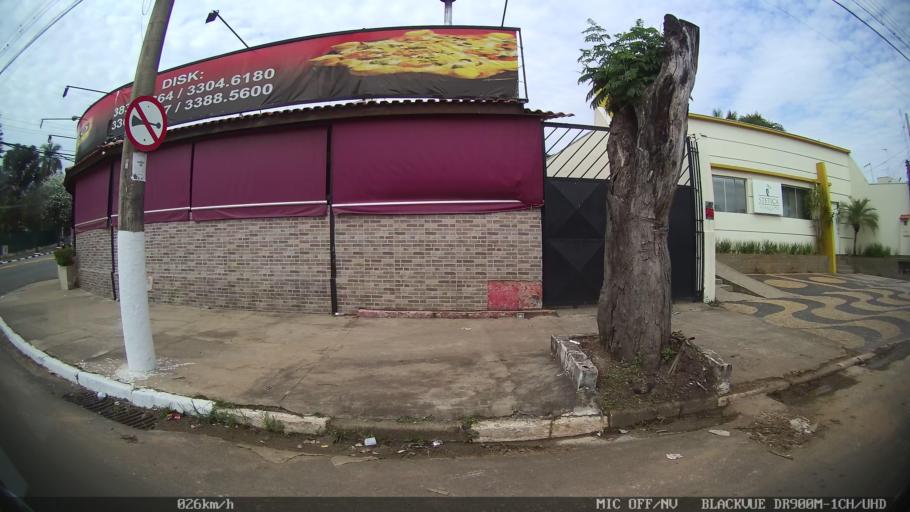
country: BR
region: Sao Paulo
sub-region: Paulinia
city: Paulinia
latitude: -22.7656
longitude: -47.1531
